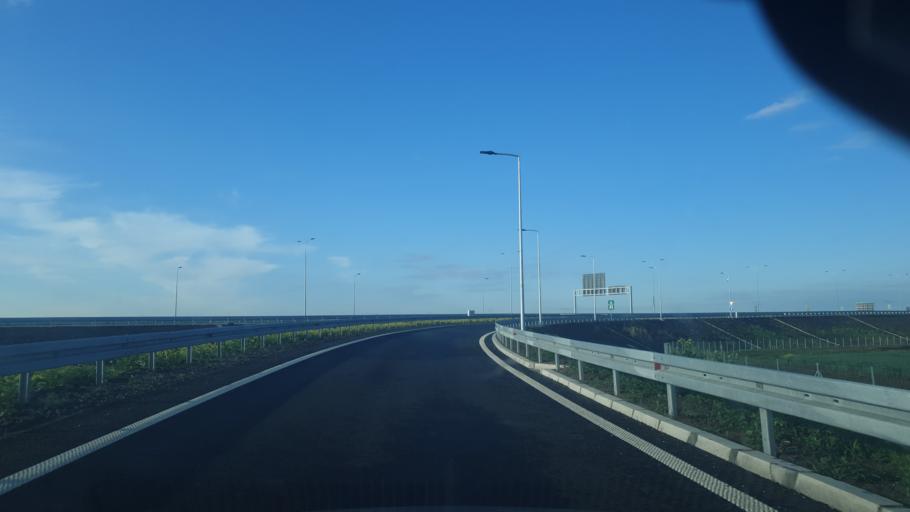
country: RS
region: Central Serbia
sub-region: Belgrade
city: Surcin
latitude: 44.7749
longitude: 20.2765
